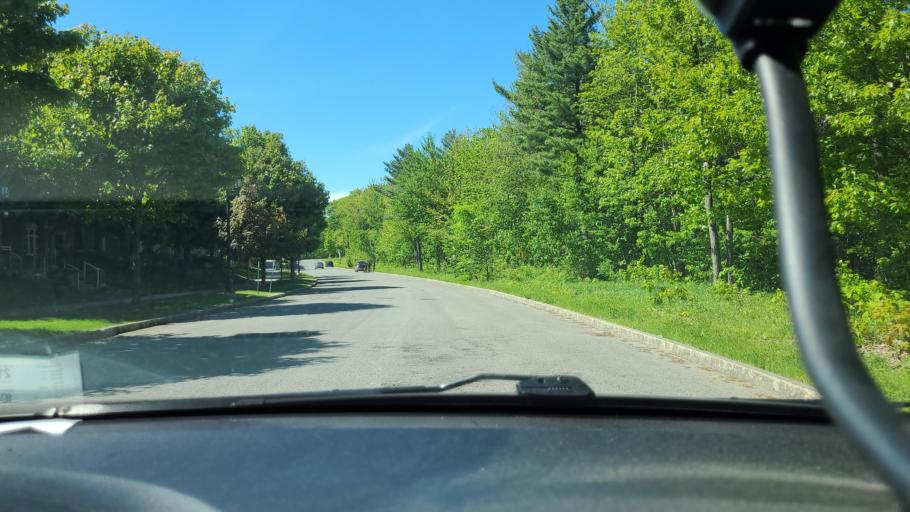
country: CA
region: Quebec
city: L'Ancienne-Lorette
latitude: 46.7548
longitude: -71.3247
